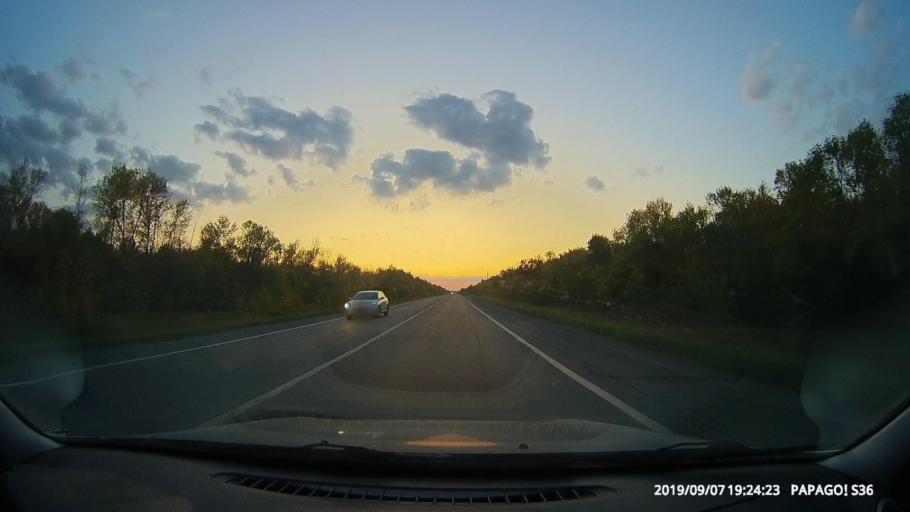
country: RU
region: Samara
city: Chapayevsk
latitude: 52.9973
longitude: 49.7734
